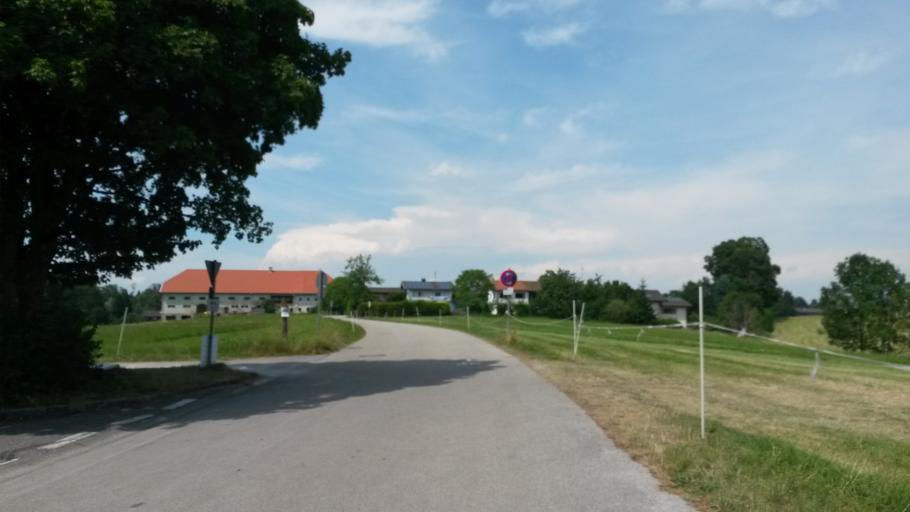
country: DE
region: Bavaria
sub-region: Upper Bavaria
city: Gstadt am Chiemsee
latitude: 47.8820
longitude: 12.3880
